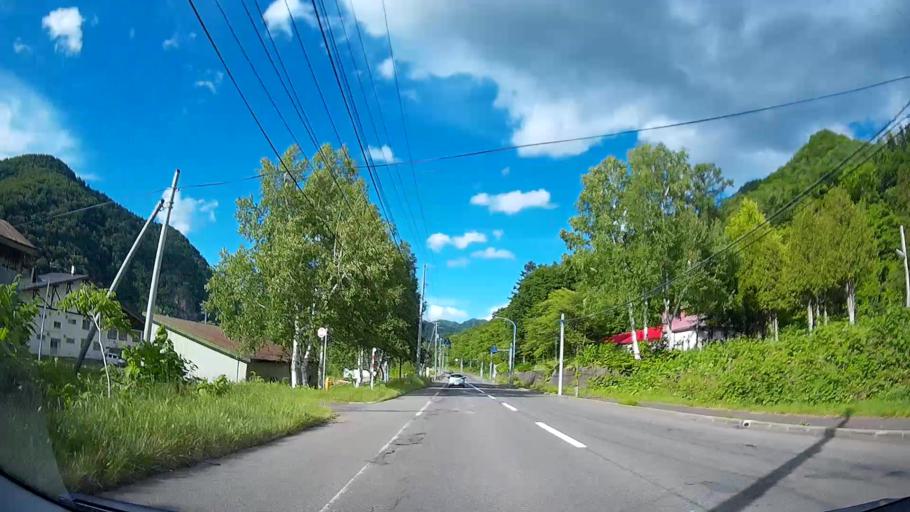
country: JP
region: Hokkaido
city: Sapporo
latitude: 42.9571
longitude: 141.1542
